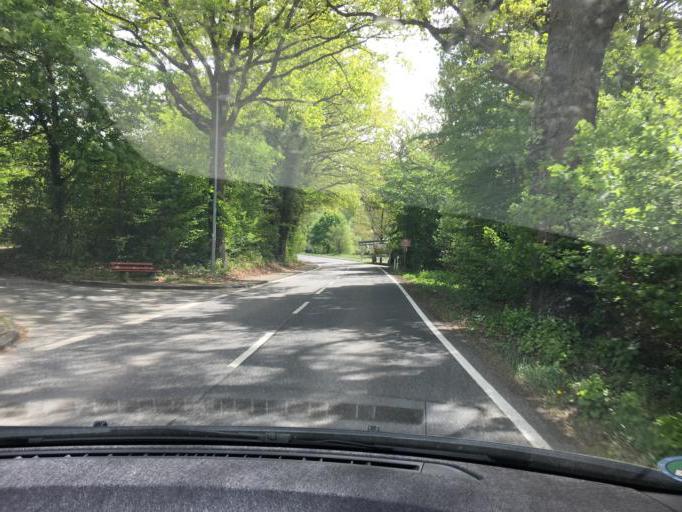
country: DE
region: North Rhine-Westphalia
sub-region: Regierungsbezirk Koln
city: Bad Munstereifel
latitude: 50.5612
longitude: 6.7681
